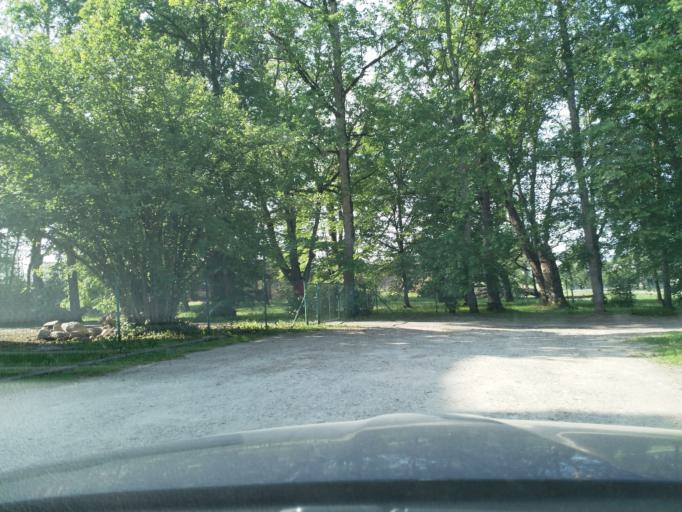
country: LV
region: Talsu Rajons
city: Sabile
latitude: 56.9502
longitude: 22.3998
